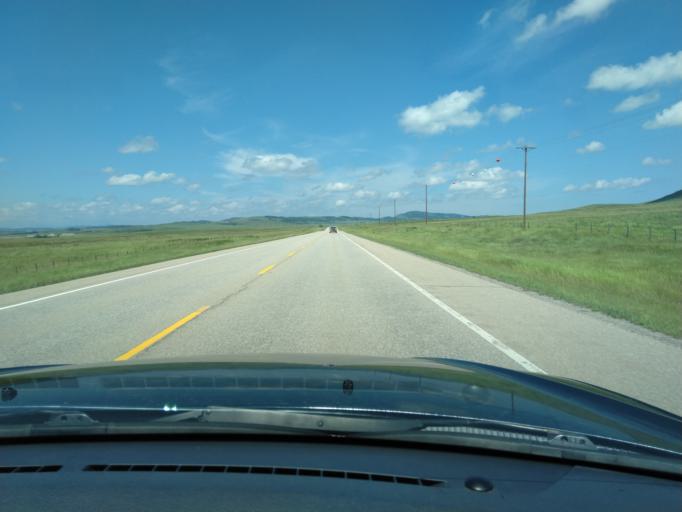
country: CA
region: Alberta
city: Cochrane
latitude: 51.2224
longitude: -114.5476
